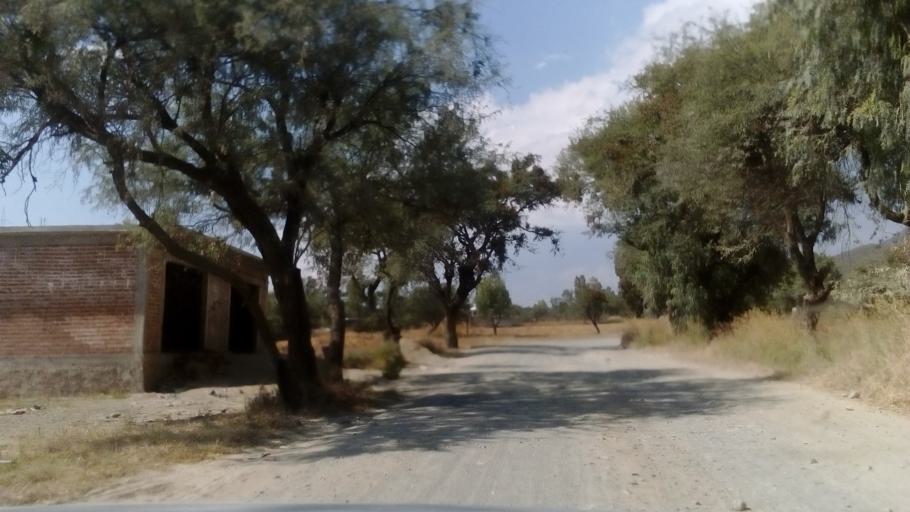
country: MX
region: Guanajuato
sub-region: Silao de la Victoria
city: San Francisco (Banos de Agua Caliente)
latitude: 21.0731
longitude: -101.4674
